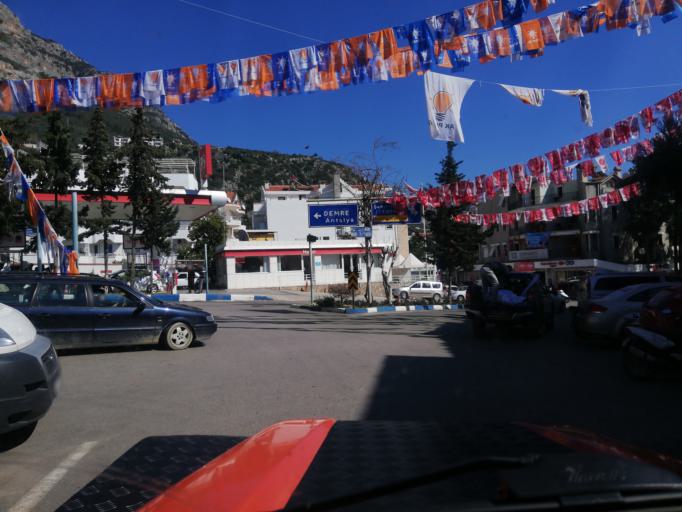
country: TR
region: Antalya
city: Kas
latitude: 36.2018
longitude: 29.6382
